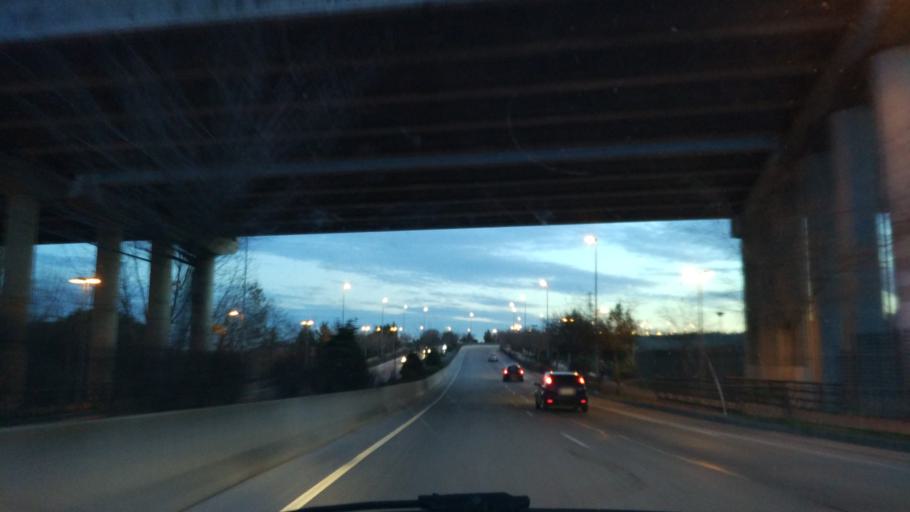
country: ES
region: Madrid
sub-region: Provincia de Madrid
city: Leganes
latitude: 40.3539
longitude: -3.7724
